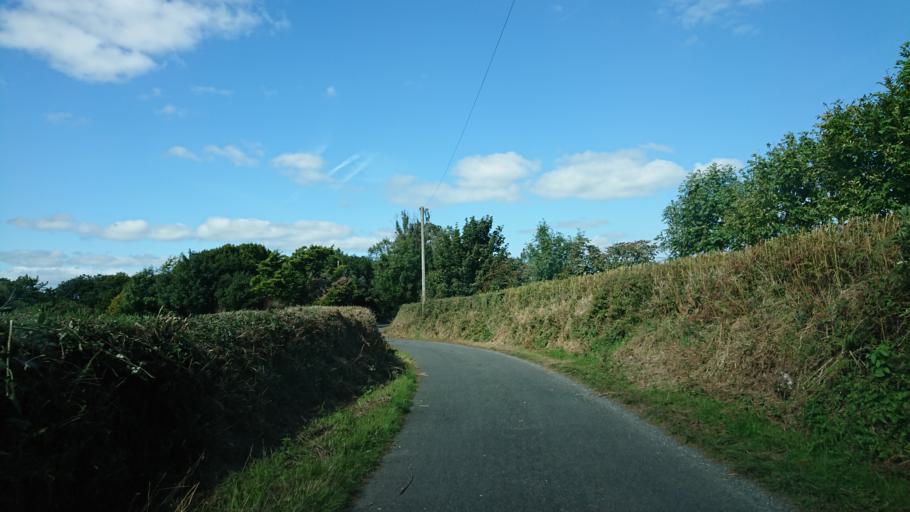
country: IE
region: Munster
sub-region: Waterford
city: Waterford
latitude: 52.2327
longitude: -7.1572
